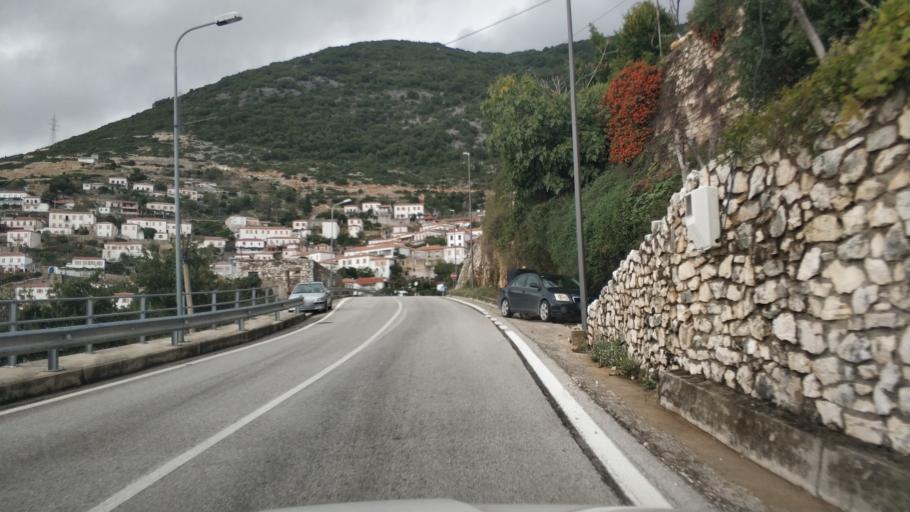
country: AL
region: Vlore
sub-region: Rrethi i Vlores
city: Himare
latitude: 40.1392
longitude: 19.6959
